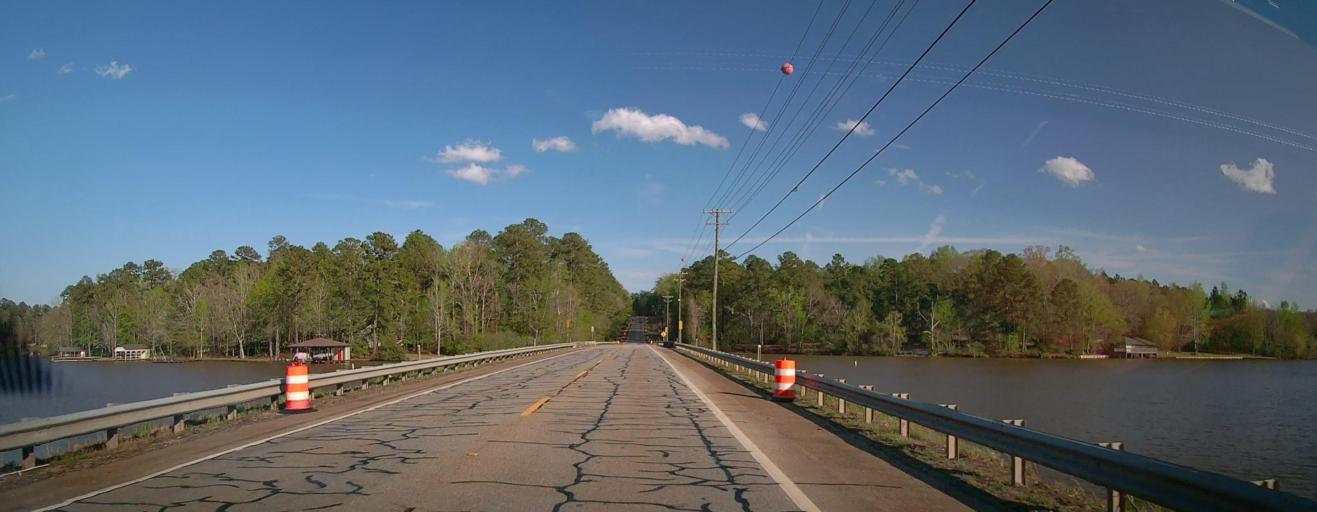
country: US
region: Georgia
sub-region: Putnam County
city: Eatonton
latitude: 33.1639
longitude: -83.3761
